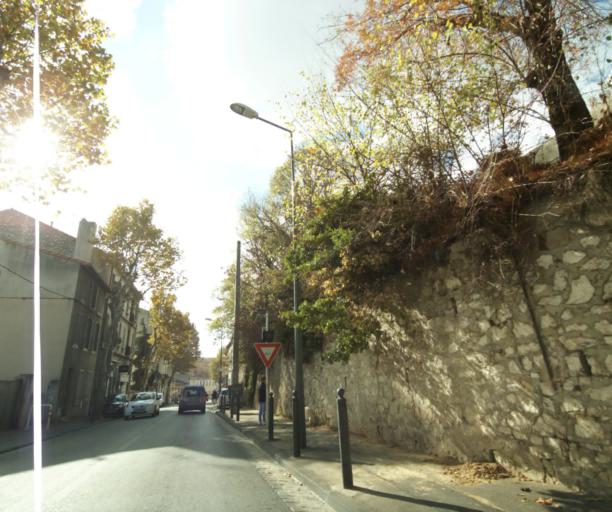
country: FR
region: Provence-Alpes-Cote d'Azur
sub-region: Departement des Bouches-du-Rhone
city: Plan-de-Cuques
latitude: 43.3358
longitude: 5.4513
